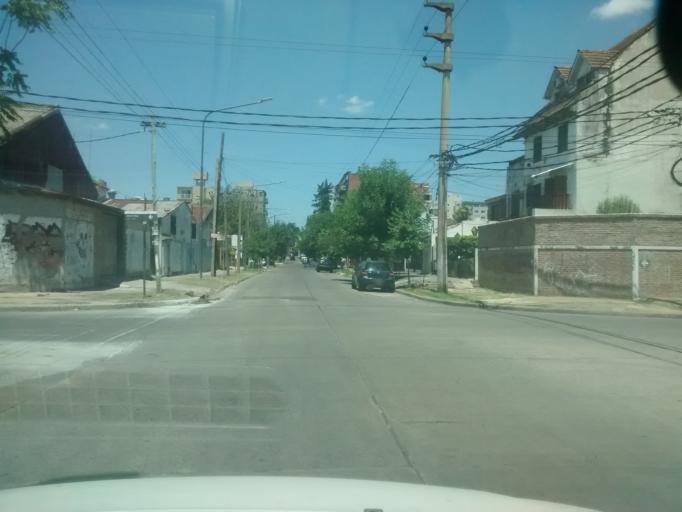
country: AR
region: Buenos Aires
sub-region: Partido de Moron
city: Moron
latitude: -34.6570
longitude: -58.6164
